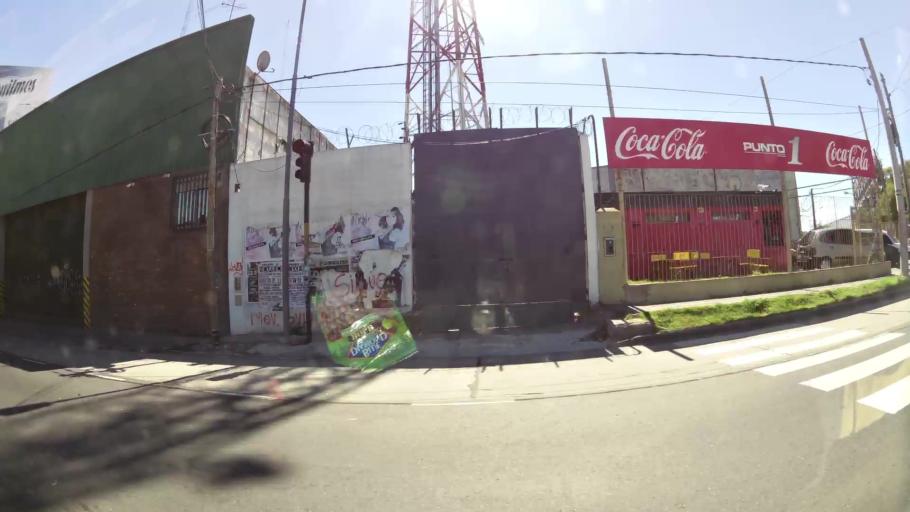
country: AR
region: Buenos Aires
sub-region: Partido de General San Martin
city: General San Martin
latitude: -34.5186
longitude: -58.5692
